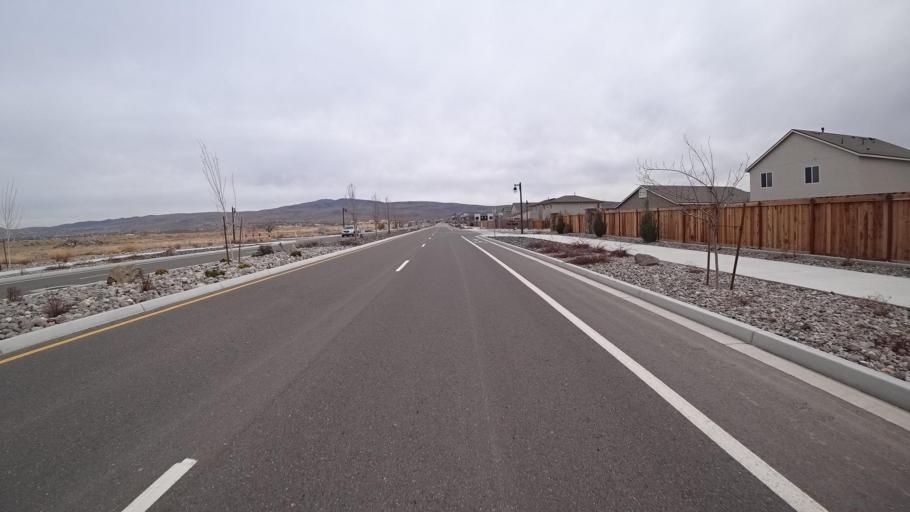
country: US
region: Nevada
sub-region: Washoe County
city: Spanish Springs
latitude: 39.6149
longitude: -119.7164
